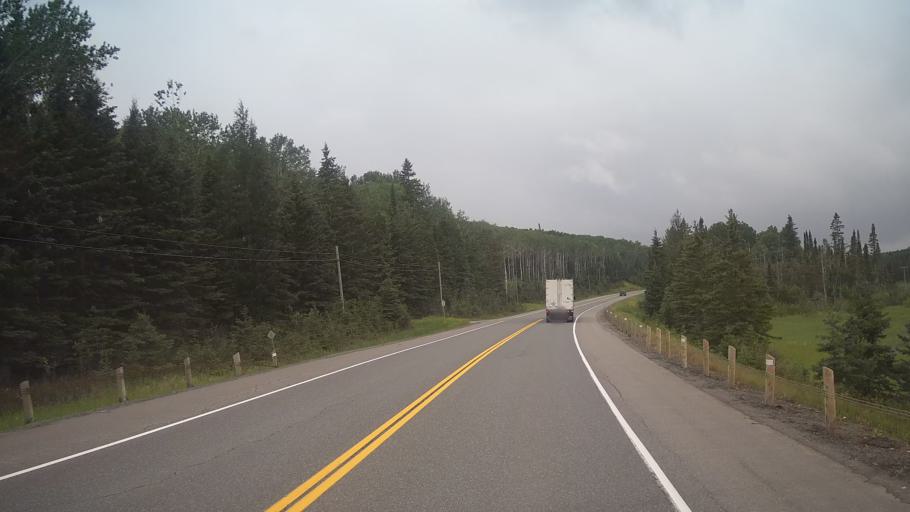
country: CA
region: Ontario
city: Neebing
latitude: 48.5821
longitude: -89.8223
